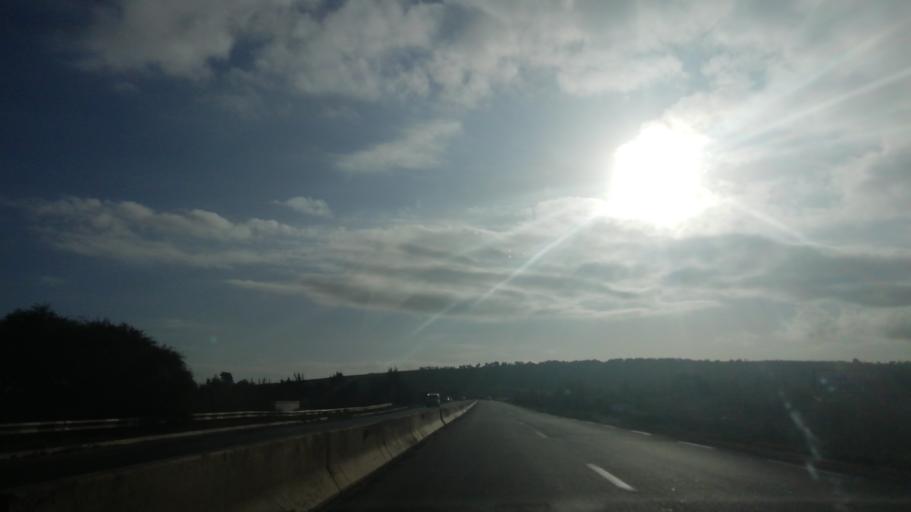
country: DZ
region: Mostaganem
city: Mostaganem
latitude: 36.0982
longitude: 0.2726
